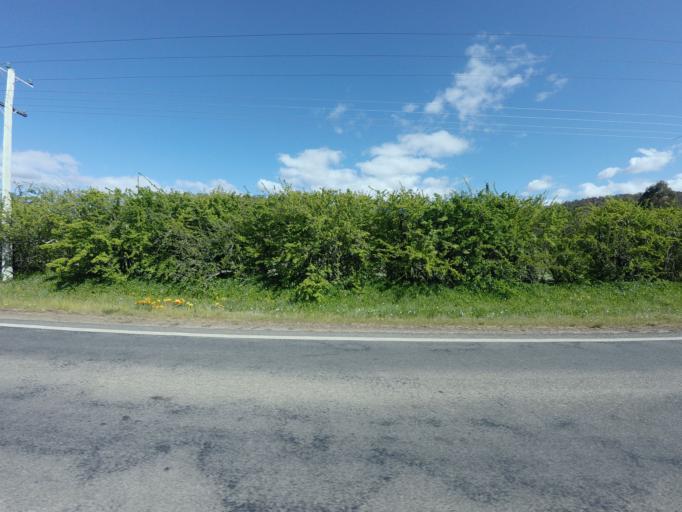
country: AU
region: Tasmania
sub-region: Derwent Valley
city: New Norfolk
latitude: -42.7782
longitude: 147.0462
